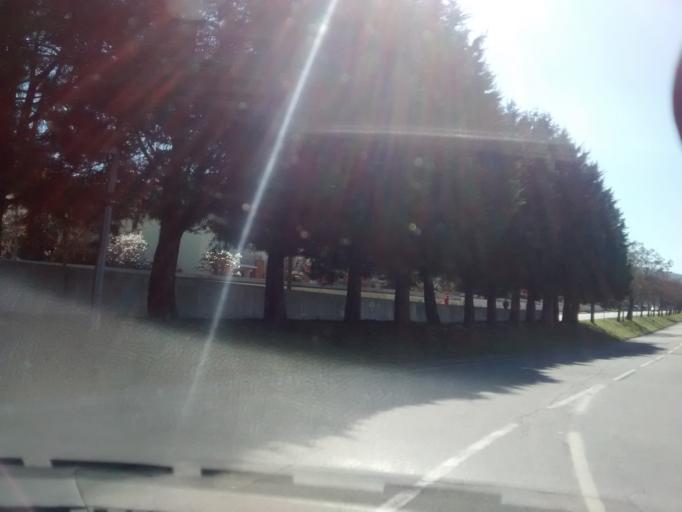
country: PT
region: Braga
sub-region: Braga
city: Braga
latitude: 41.5558
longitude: -8.3950
